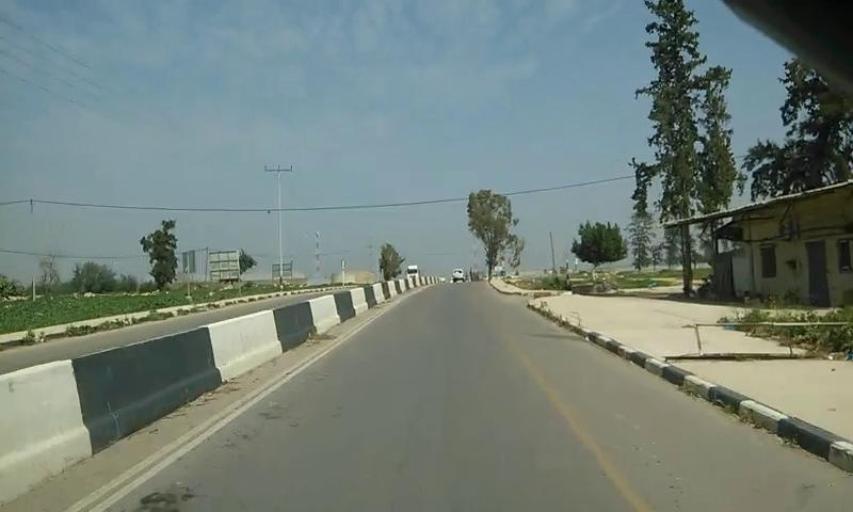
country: PS
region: West Bank
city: Al Jalamah
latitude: 32.5065
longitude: 35.3051
